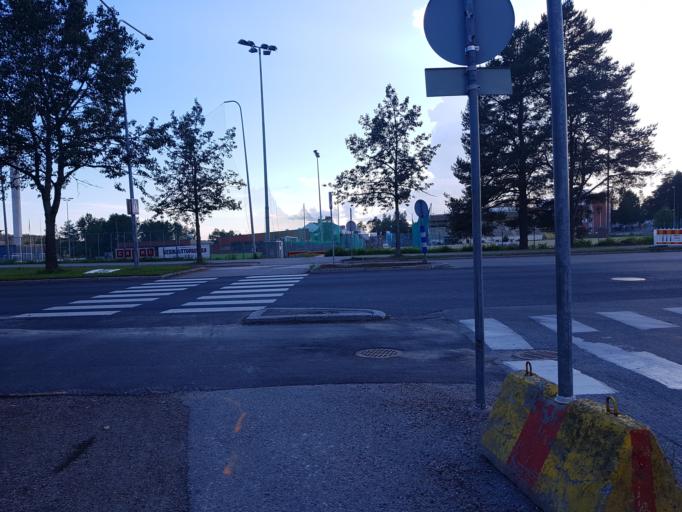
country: FI
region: Kainuu
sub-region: Kajaani
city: Kajaani
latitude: 64.2204
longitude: 27.7296
